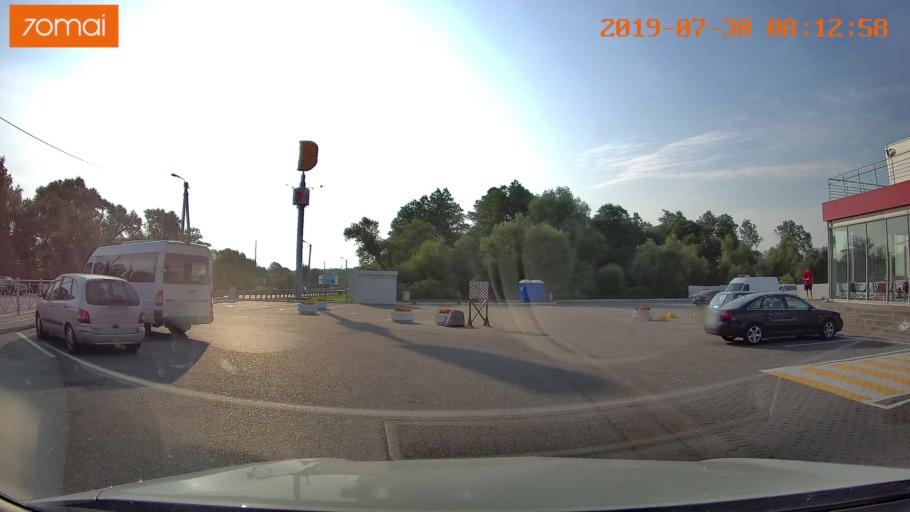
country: RU
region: Kaliningrad
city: Gvardeysk
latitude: 54.6505
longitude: 21.3413
